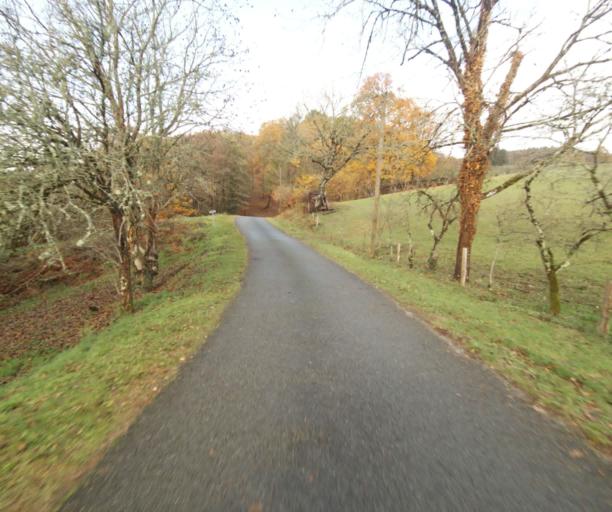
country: FR
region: Limousin
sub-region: Departement de la Correze
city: Cornil
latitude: 45.2214
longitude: 1.6599
